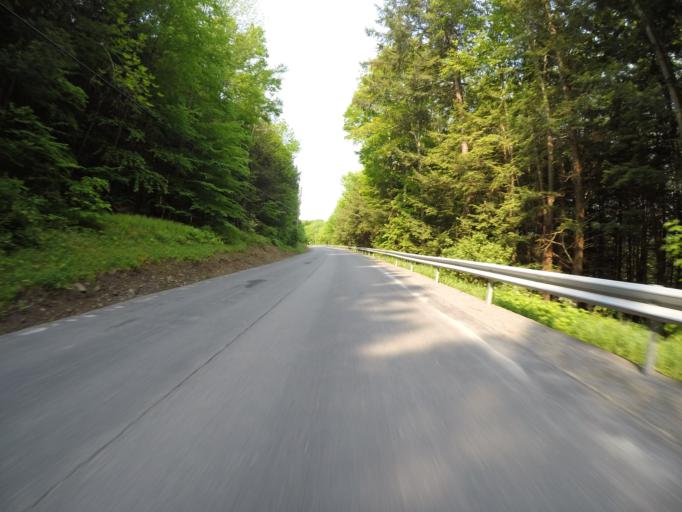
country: US
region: New York
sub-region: Sullivan County
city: Livingston Manor
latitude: 42.1136
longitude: -74.7301
